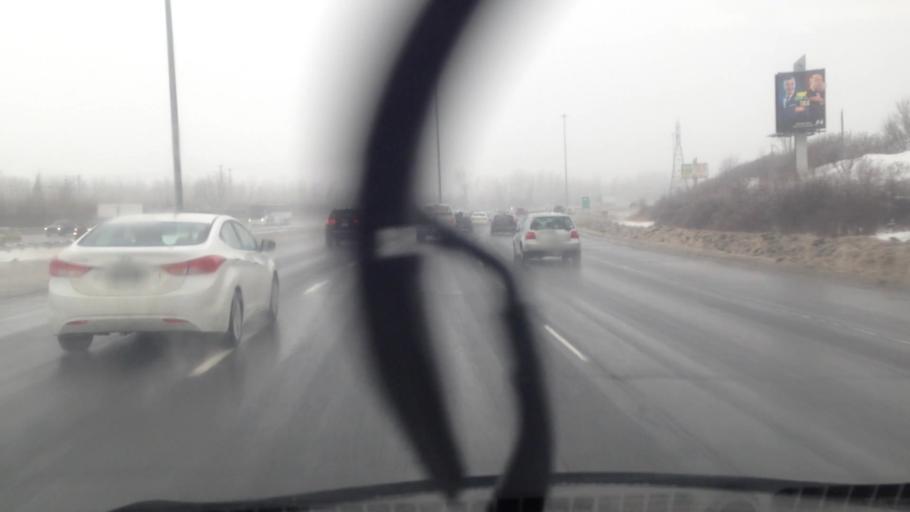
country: CA
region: Quebec
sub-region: Laurentides
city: Boisbriand
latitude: 45.5911
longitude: -73.7992
